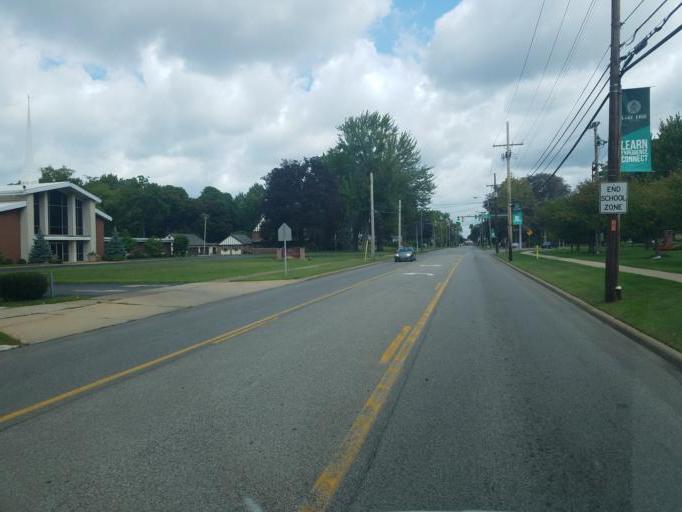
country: US
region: Ohio
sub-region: Lake County
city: Painesville
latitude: 41.7181
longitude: -81.2536
